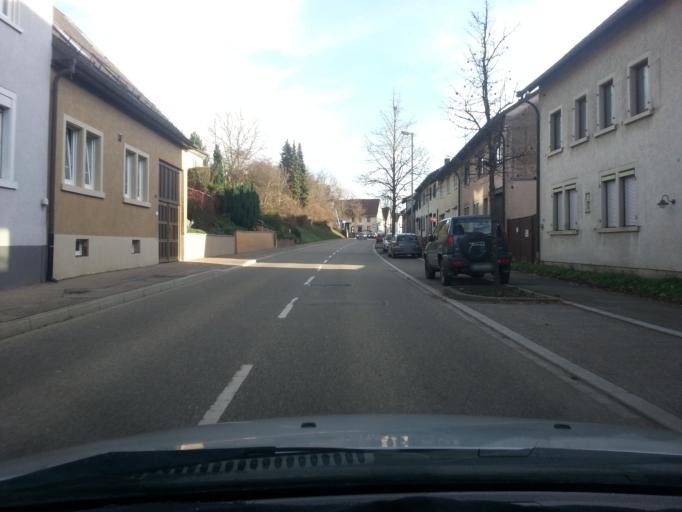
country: DE
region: Baden-Wuerttemberg
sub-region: Karlsruhe Region
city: Ostringen
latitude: 49.1809
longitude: 8.7432
